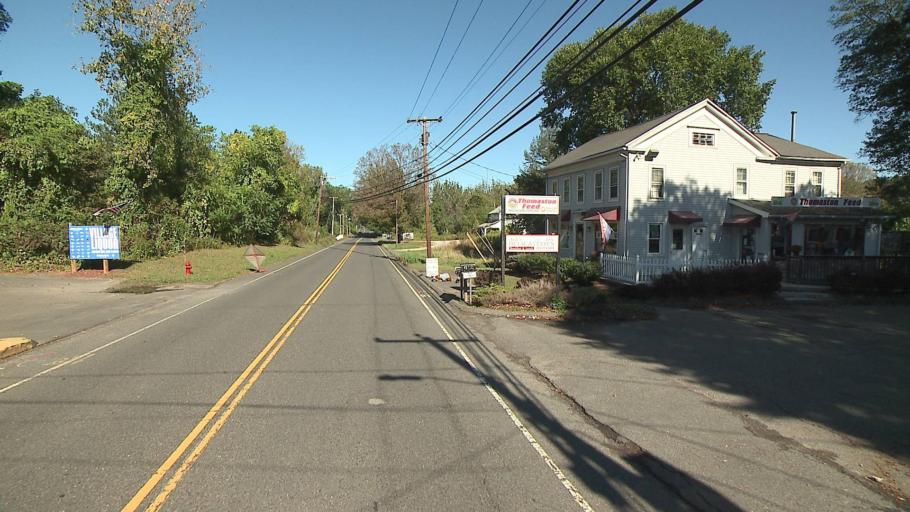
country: US
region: Connecticut
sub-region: Litchfield County
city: New Milford
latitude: 41.4845
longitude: -73.4107
